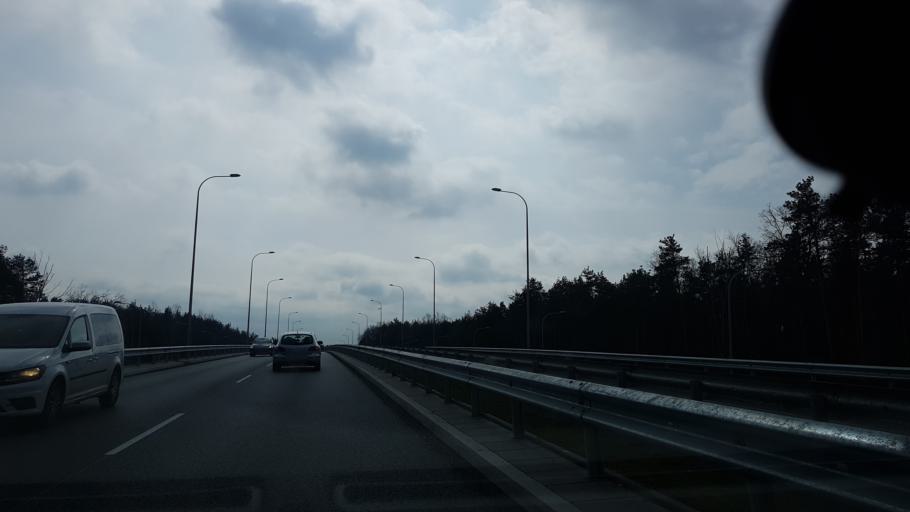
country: PL
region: Masovian Voivodeship
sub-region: Warszawa
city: Rembertow
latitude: 52.2702
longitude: 21.1439
